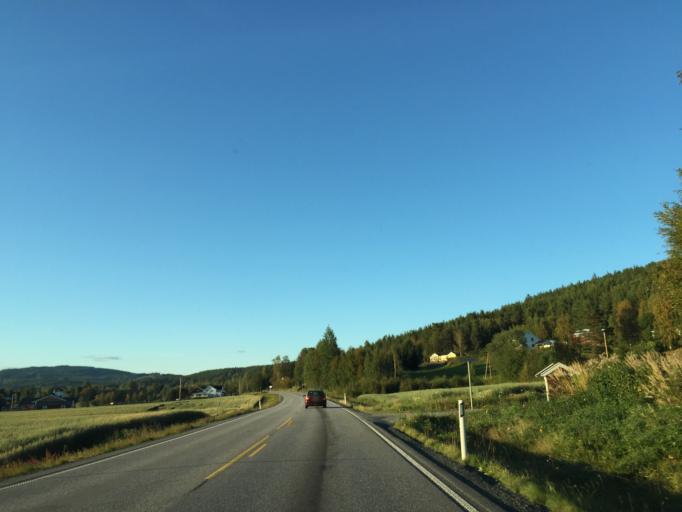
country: NO
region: Hedmark
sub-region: Nord-Odal
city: Sand
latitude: 60.4239
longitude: 11.5131
